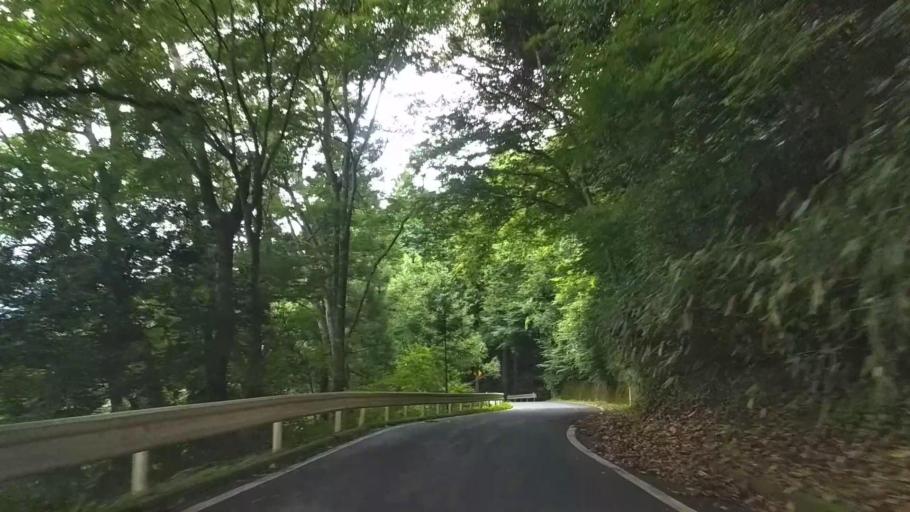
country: JP
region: Shizuoka
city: Gotemba
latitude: 35.3285
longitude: 138.9836
